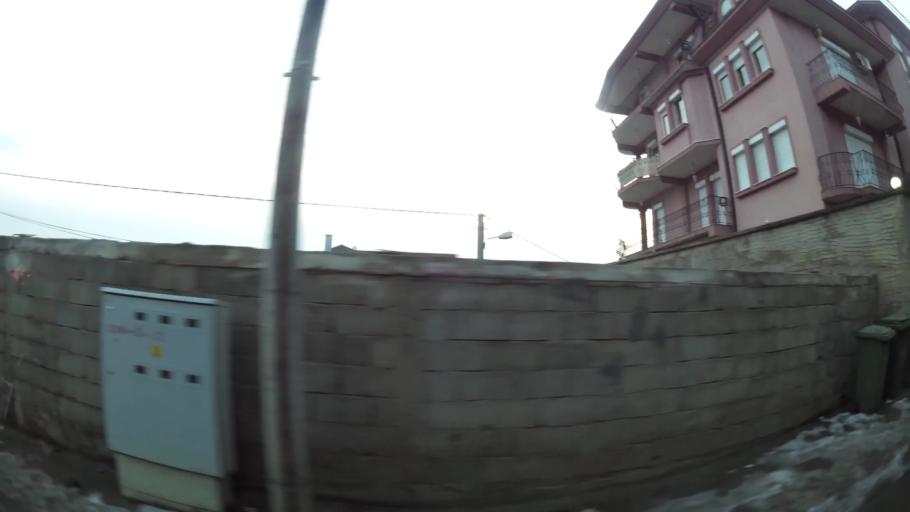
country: MK
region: Aracinovo
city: Arachinovo
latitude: 42.0285
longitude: 21.5605
